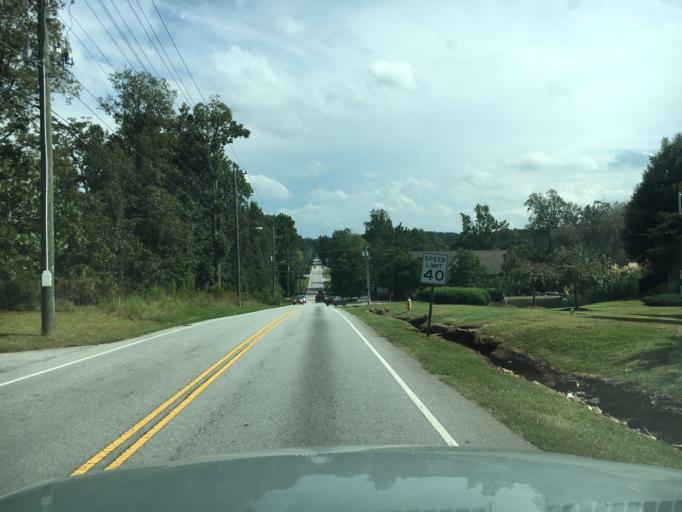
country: US
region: South Carolina
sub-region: Greenville County
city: Wade Hampton
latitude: 34.8535
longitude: -82.3198
